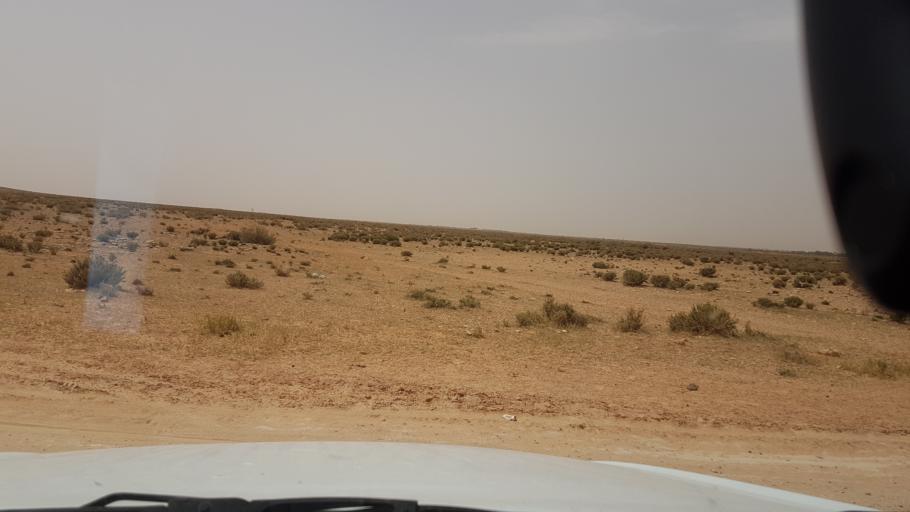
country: TN
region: Madanin
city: Medenine
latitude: 33.2868
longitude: 10.5962
